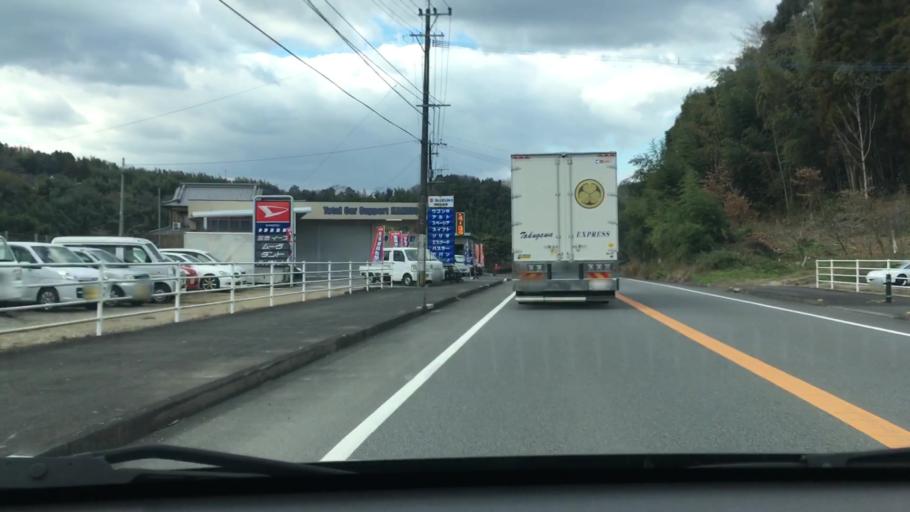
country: JP
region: Oita
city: Usuki
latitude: 33.0657
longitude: 131.6579
